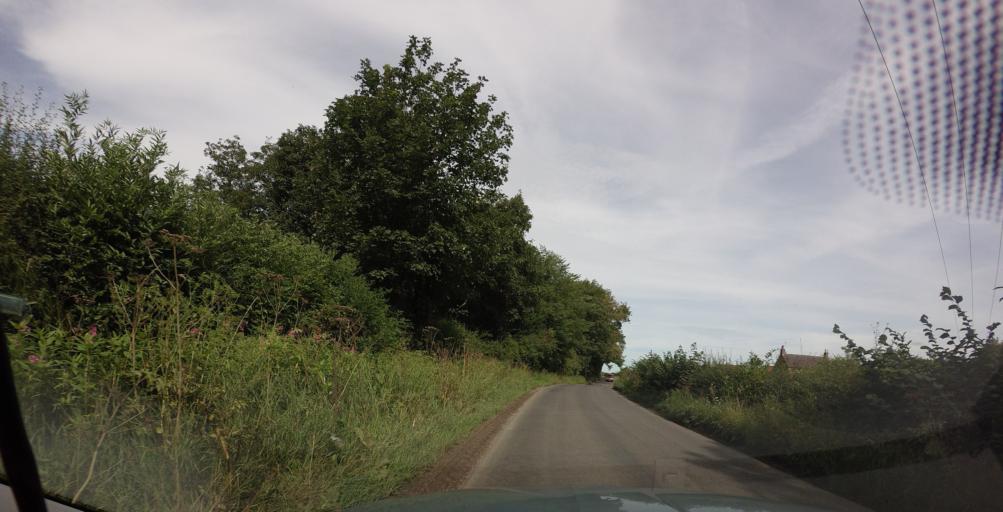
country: GB
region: England
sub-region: North Yorkshire
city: Ripon
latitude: 54.0997
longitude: -1.5141
